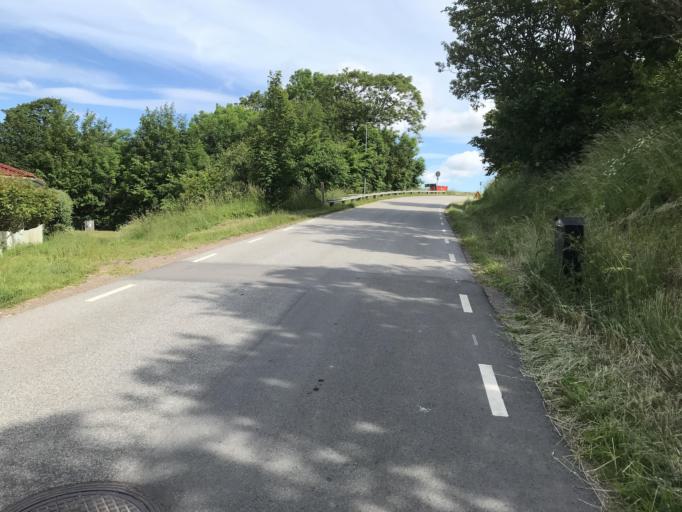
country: SE
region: Skane
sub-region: Helsingborg
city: Rydeback
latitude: 55.9429
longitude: 12.7714
